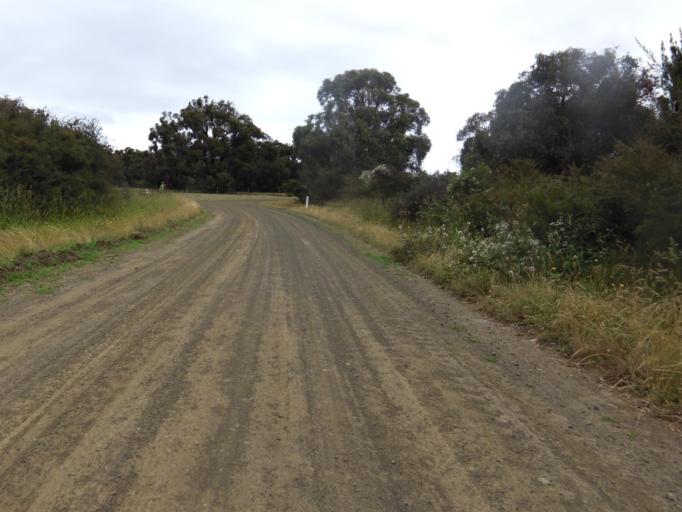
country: AU
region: Victoria
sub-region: Bass Coast
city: Cowes
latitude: -38.3890
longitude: 145.3862
